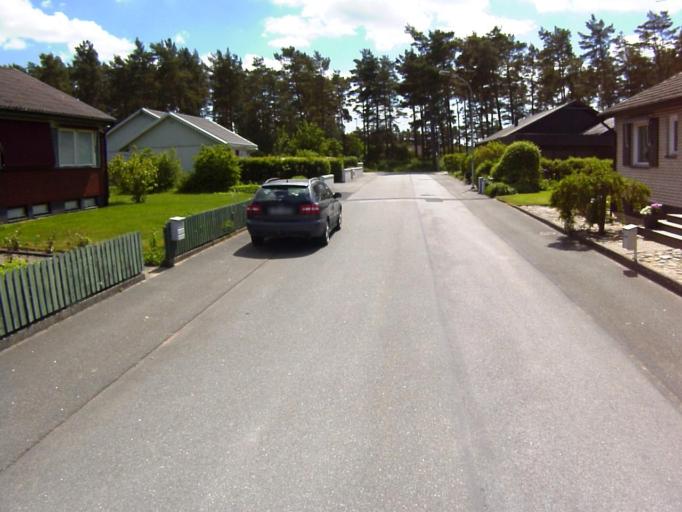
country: SE
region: Skane
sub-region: Kristianstads Kommun
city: Ahus
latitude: 55.9444
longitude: 14.2734
